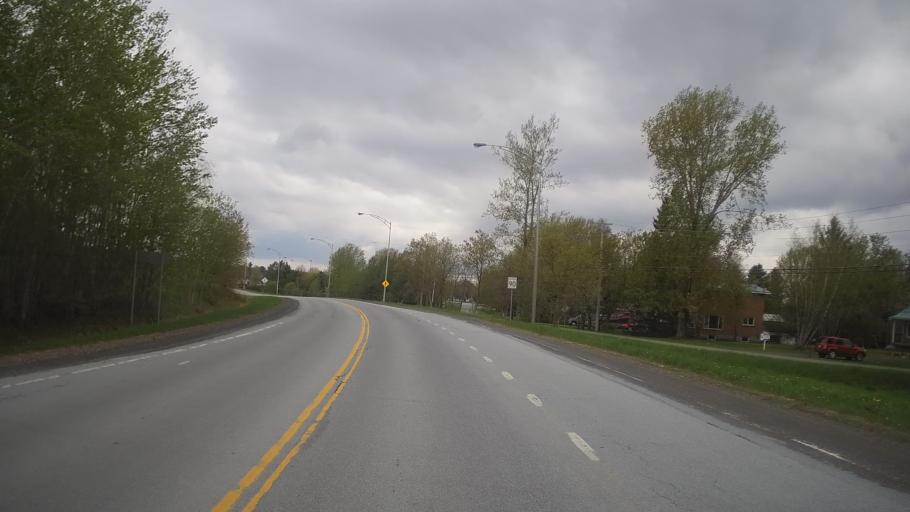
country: CA
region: Quebec
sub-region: Monteregie
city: Farnham
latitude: 45.2705
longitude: -72.9496
